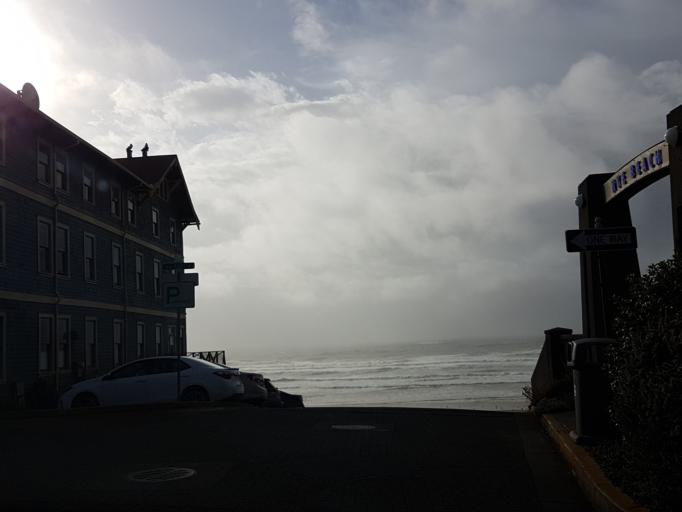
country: US
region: Oregon
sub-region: Lincoln County
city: Newport
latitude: 44.6384
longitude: -124.0618
